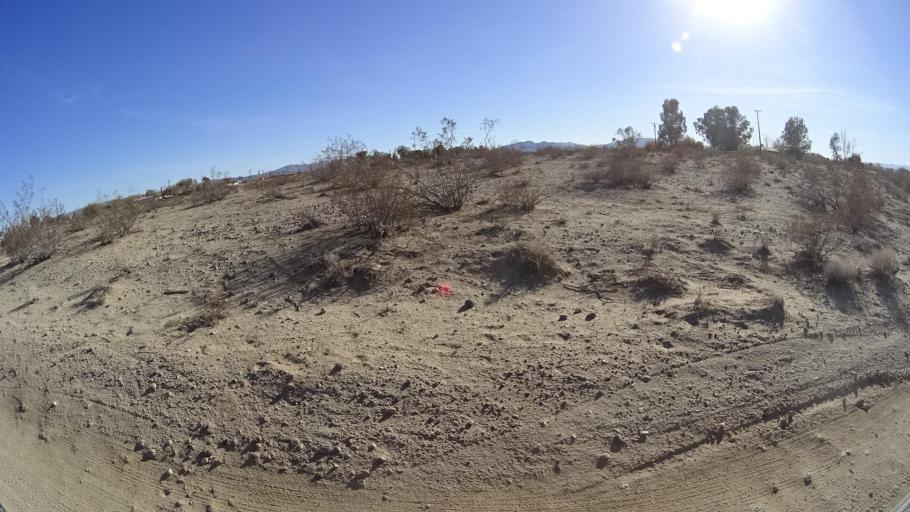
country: US
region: California
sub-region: Kern County
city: China Lake Acres
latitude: 35.6375
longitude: -117.7604
